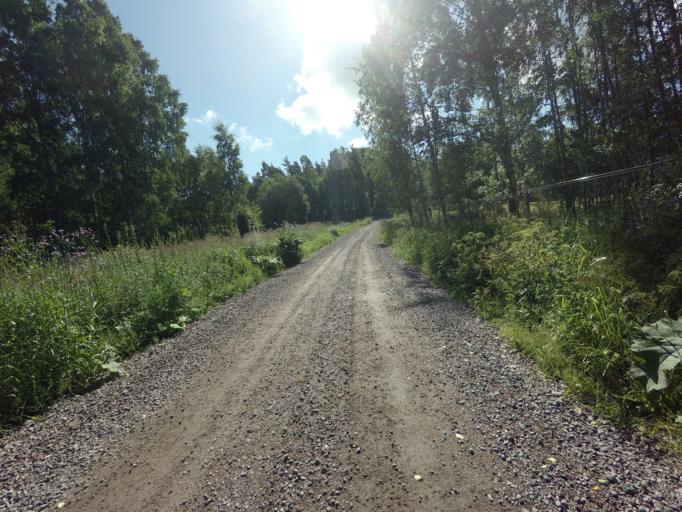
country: FI
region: Uusimaa
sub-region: Helsinki
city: Espoo
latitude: 60.1494
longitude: 24.6118
